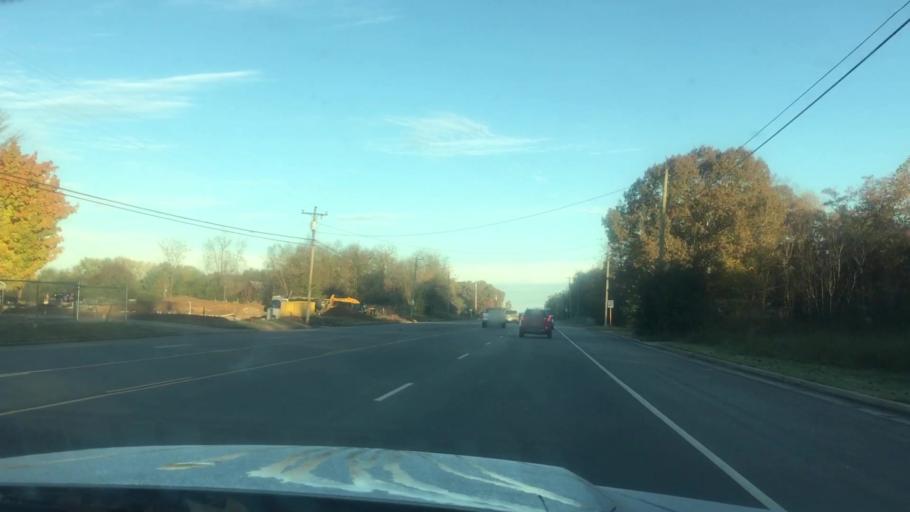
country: US
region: Tennessee
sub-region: Franklin County
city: Estill Springs
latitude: 35.2846
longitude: -86.1406
